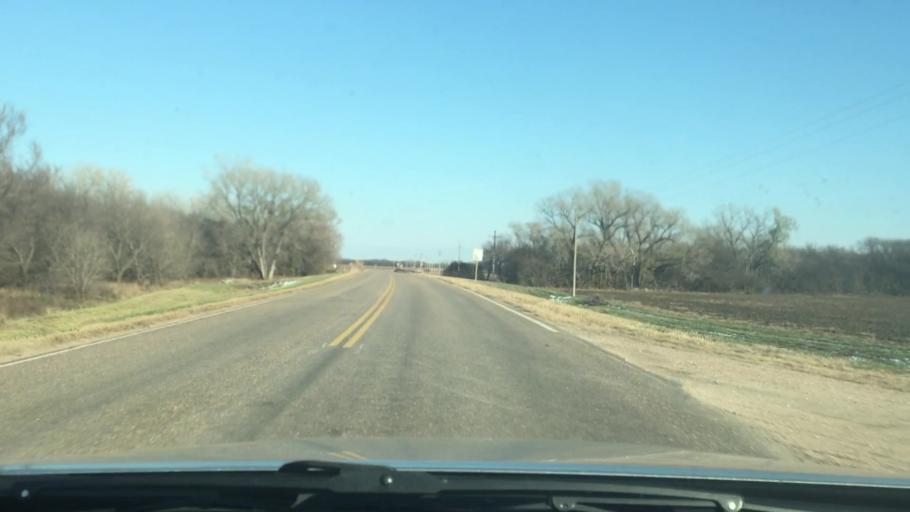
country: US
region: Kansas
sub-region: Rice County
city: Lyons
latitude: 38.2892
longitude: -98.1464
